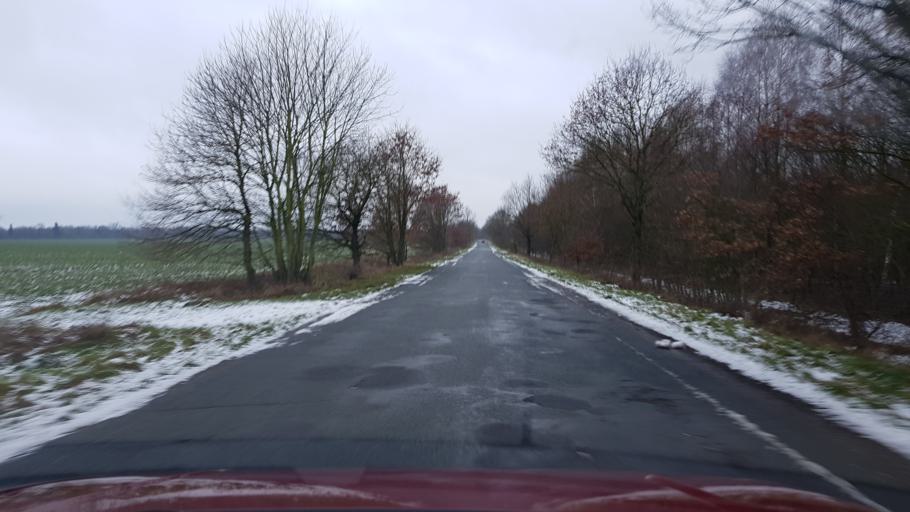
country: PL
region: West Pomeranian Voivodeship
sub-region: Powiat gryficki
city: Ploty
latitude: 53.6871
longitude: 15.2436
